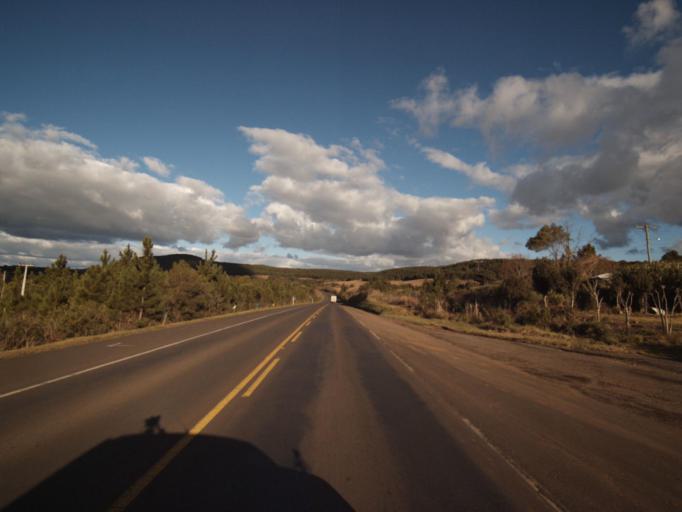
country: BR
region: Santa Catarina
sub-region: Campos Novos
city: Campos Novos
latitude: -27.3542
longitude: -51.3332
